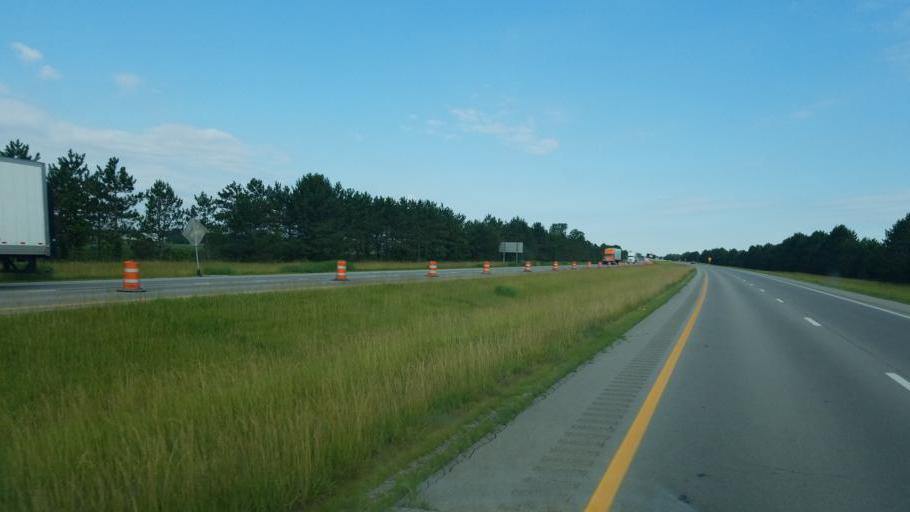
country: US
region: Ohio
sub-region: Wyandot County
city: Carey
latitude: 40.9497
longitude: -83.4219
